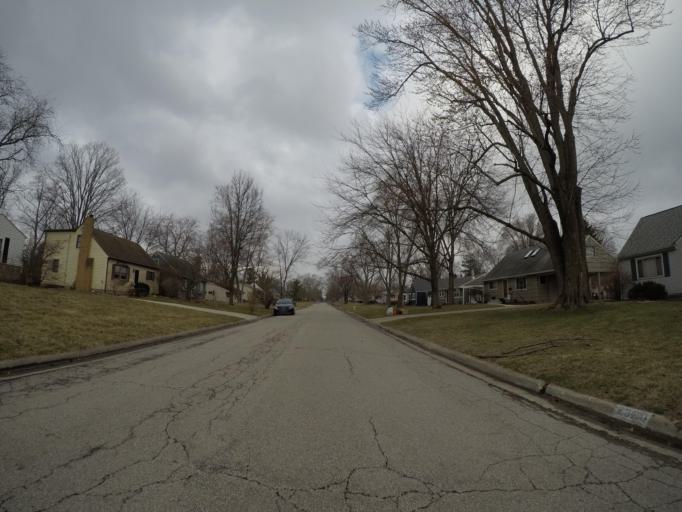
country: US
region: Ohio
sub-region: Franklin County
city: Upper Arlington
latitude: 40.0263
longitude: -83.0787
